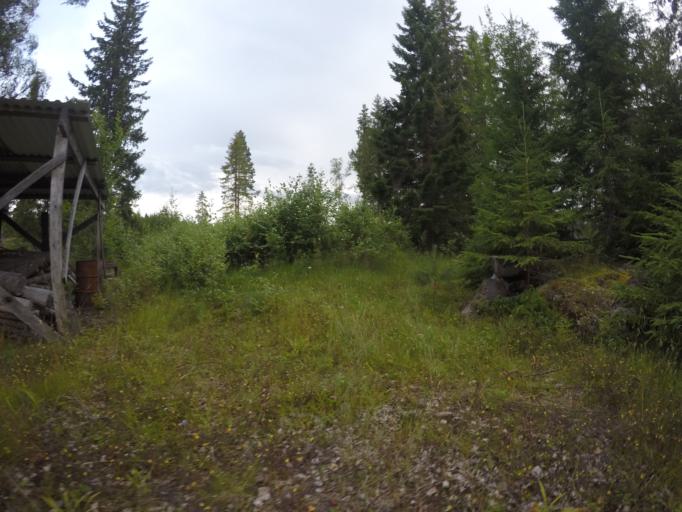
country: SE
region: OErebro
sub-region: Hallefors Kommun
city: Haellefors
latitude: 60.0403
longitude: 14.5030
